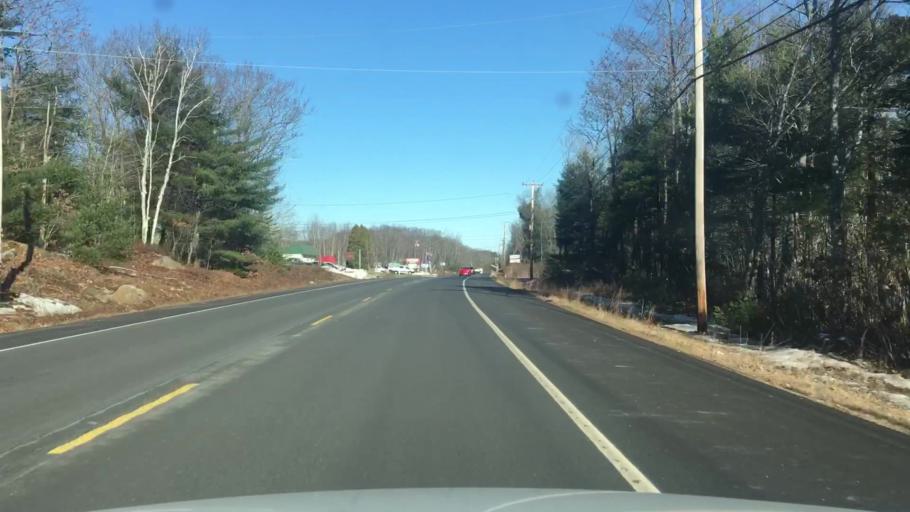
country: US
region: Maine
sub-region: York County
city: Arundel
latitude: 43.4384
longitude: -70.5036
